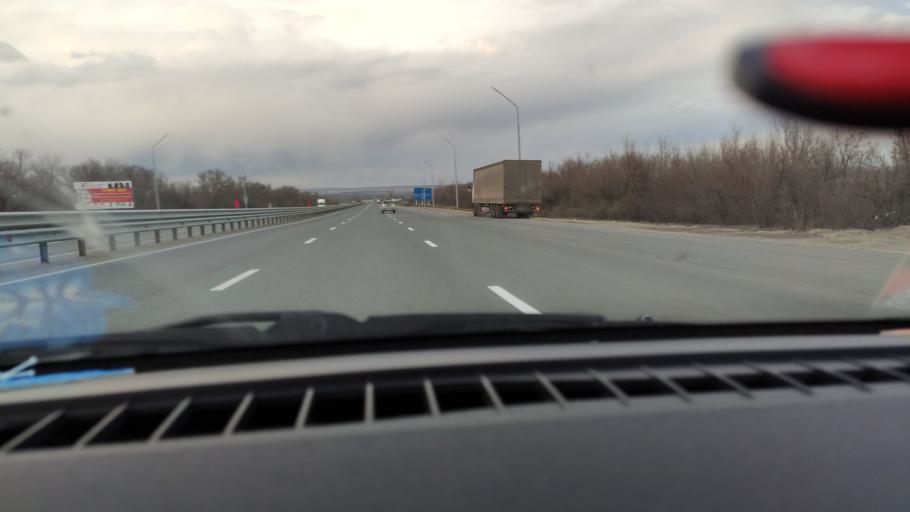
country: RU
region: Saratov
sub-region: Saratovskiy Rayon
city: Saratov
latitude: 51.6653
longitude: 45.9997
